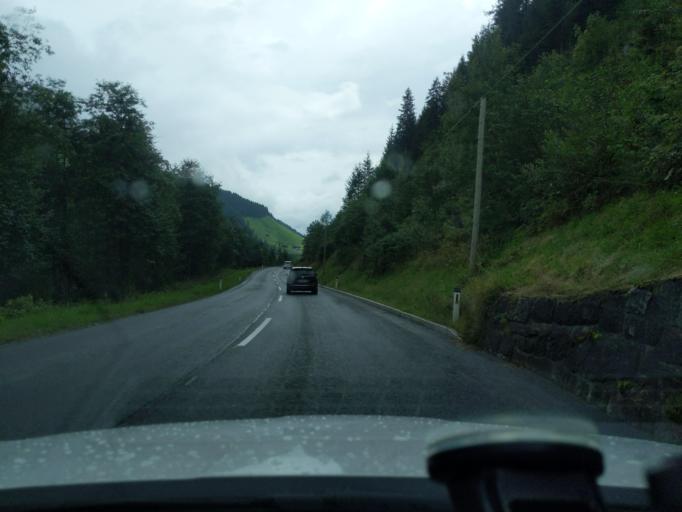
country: AT
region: Tyrol
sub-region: Politischer Bezirk Schwaz
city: Schwendau
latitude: 47.1608
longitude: 11.7495
